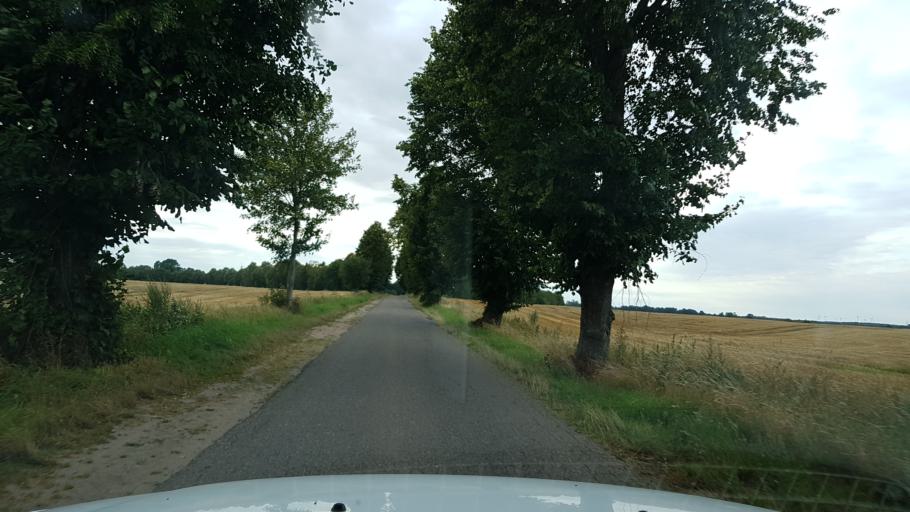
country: PL
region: West Pomeranian Voivodeship
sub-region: Powiat bialogardzki
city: Karlino
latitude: 54.1142
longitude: 15.8765
